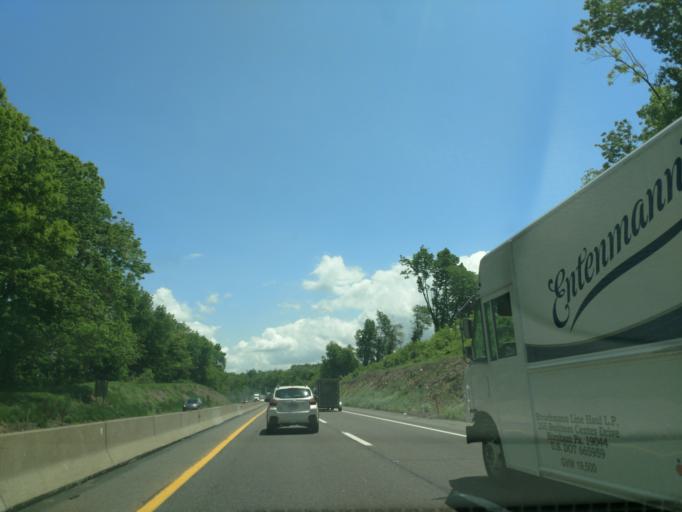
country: US
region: Pennsylvania
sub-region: Chester County
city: Elverson
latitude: 40.1299
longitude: -75.7897
